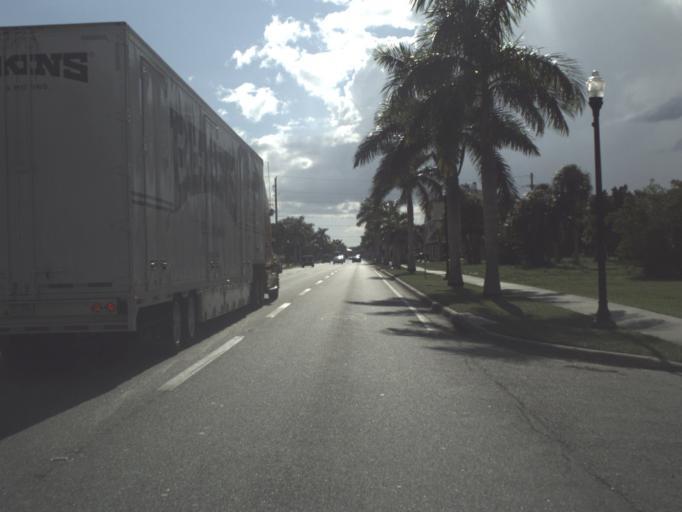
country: US
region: Florida
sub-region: Charlotte County
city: Punta Gorda
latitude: 26.9406
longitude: -82.0420
